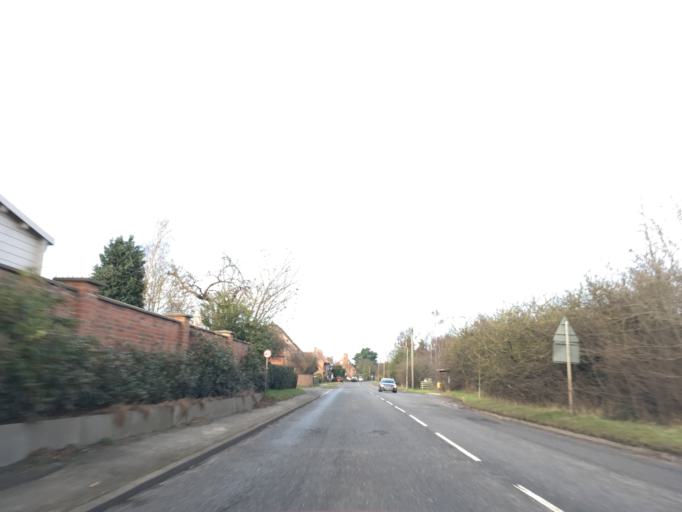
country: GB
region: England
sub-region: Nottinghamshire
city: South Collingham
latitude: 53.1730
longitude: -0.7647
